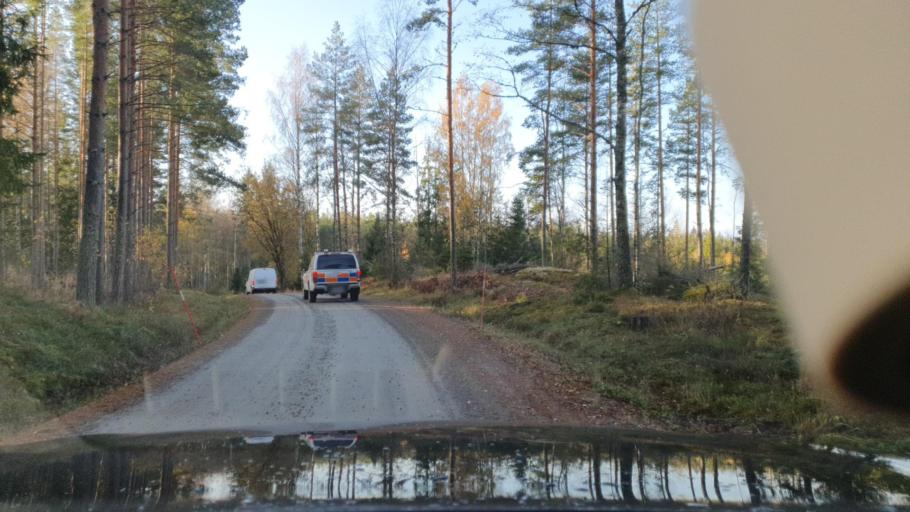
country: SE
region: Vaermland
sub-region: Grums Kommun
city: Grums
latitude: 59.4692
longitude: 12.9234
